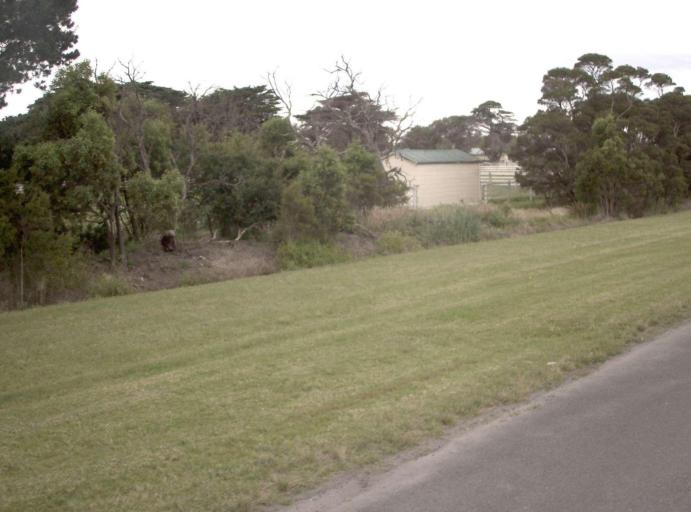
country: AU
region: Victoria
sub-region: Cardinia
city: Koo-Wee-Rup
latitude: -38.2199
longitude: 145.5080
